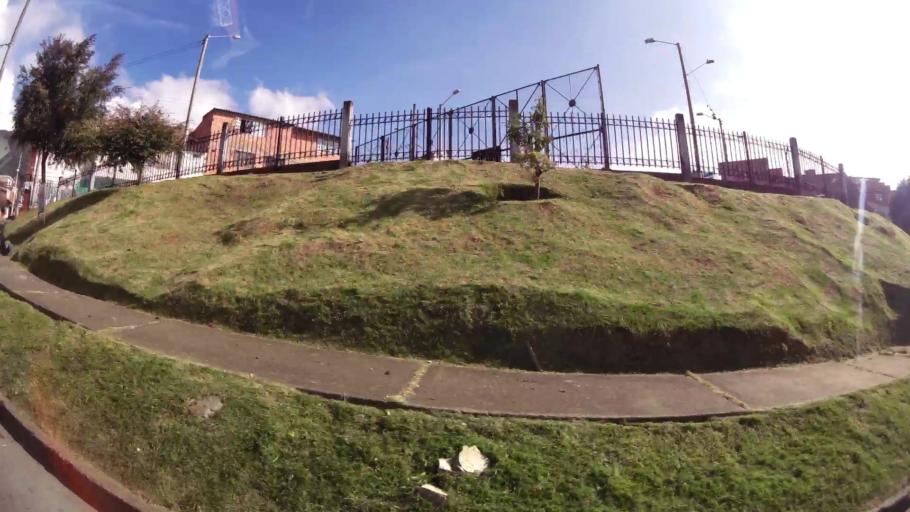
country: CO
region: Bogota D.C.
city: Bogota
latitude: 4.5386
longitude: -74.0874
